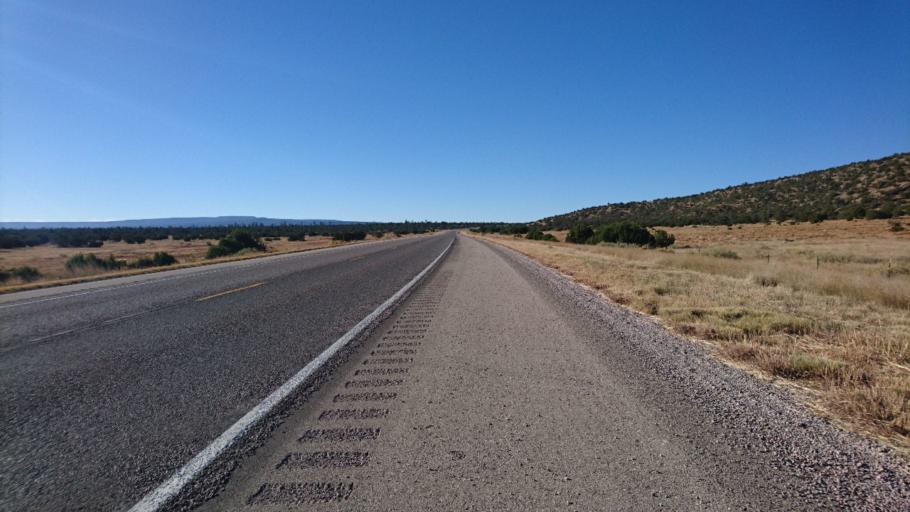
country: US
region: New Mexico
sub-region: Cibola County
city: Grants
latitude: 34.9729
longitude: -107.9124
